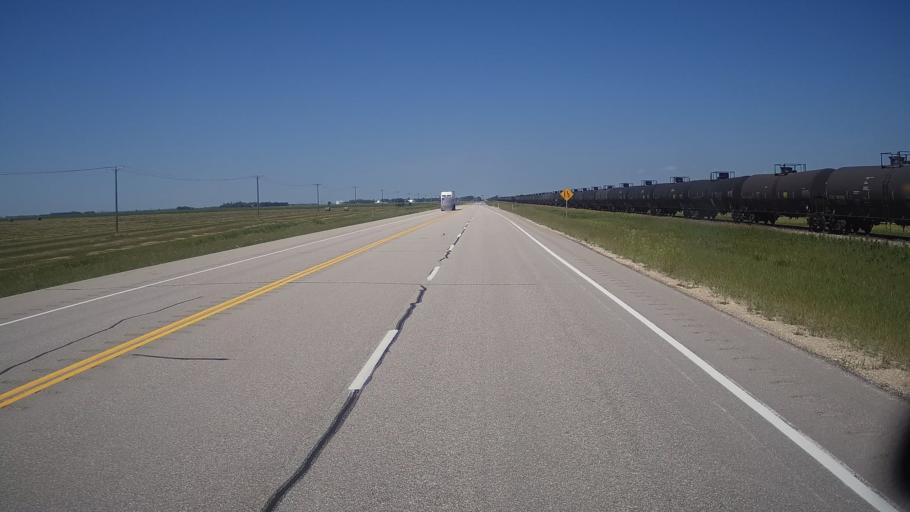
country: CA
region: Manitoba
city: Stonewall
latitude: 50.1095
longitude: -97.5114
